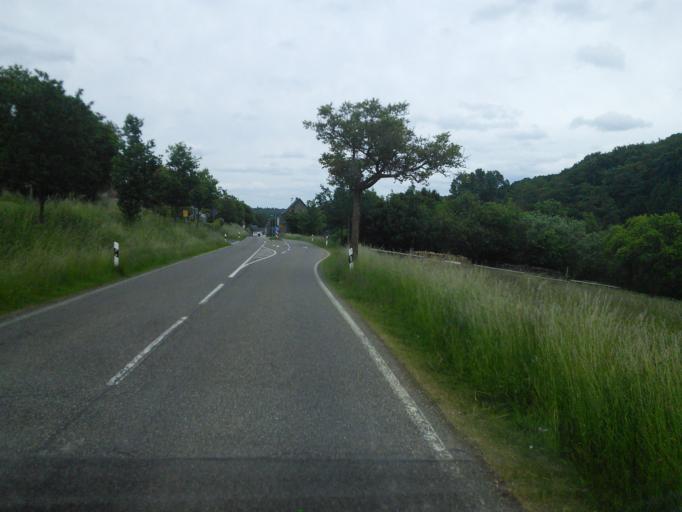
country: DE
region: Rheinland-Pfalz
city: Berg
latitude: 50.5859
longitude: 6.9232
